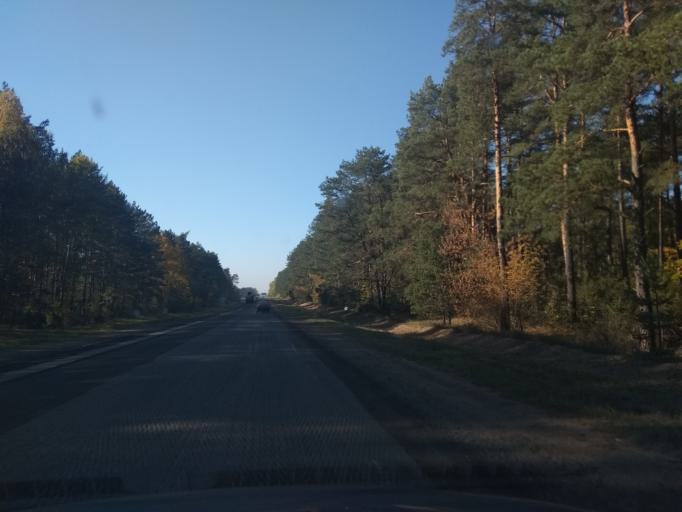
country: BY
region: Grodnenskaya
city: Zhyrovichy
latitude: 53.0617
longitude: 25.4231
